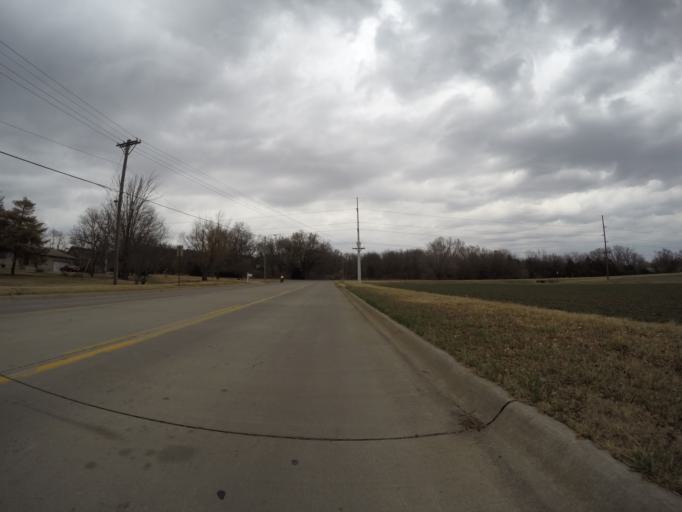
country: US
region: Kansas
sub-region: Riley County
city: Manhattan
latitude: 39.2177
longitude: -96.6074
